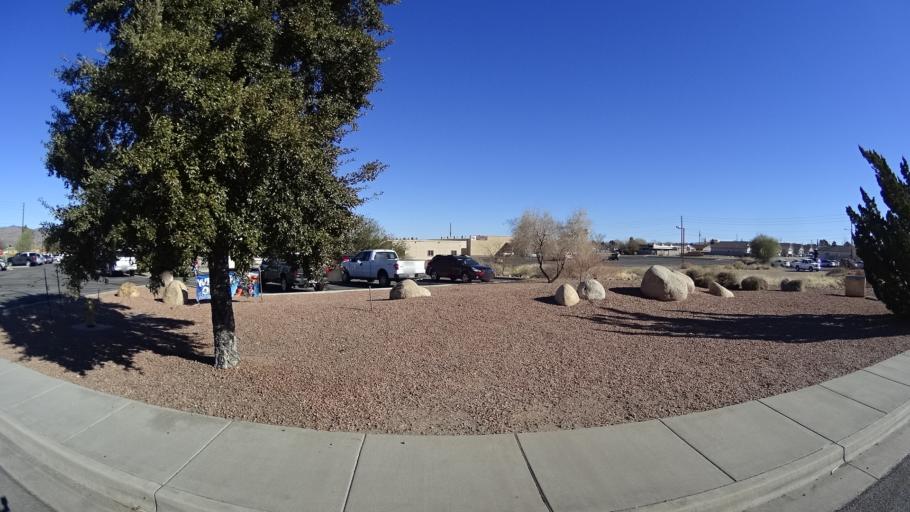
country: US
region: Arizona
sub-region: Mohave County
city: Kingman
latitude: 35.1924
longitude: -114.0259
